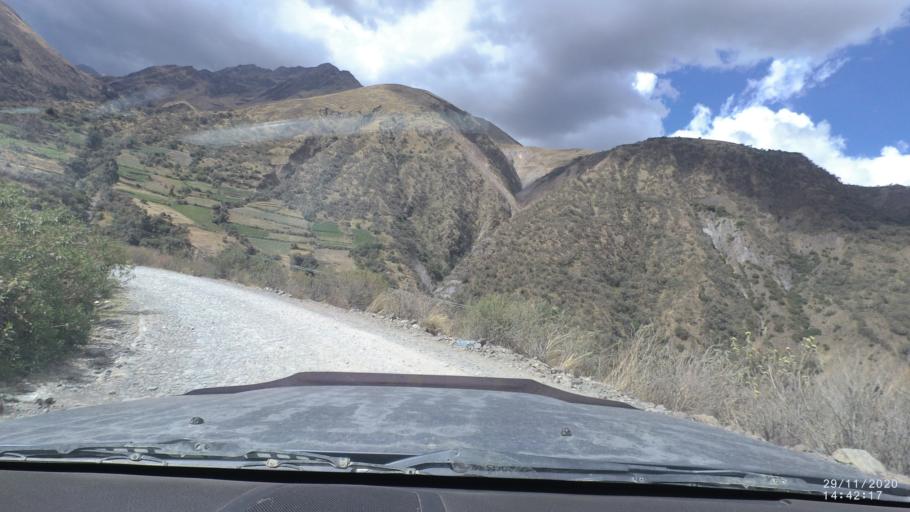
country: BO
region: Cochabamba
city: Sipe Sipe
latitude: -17.2780
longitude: -66.3212
